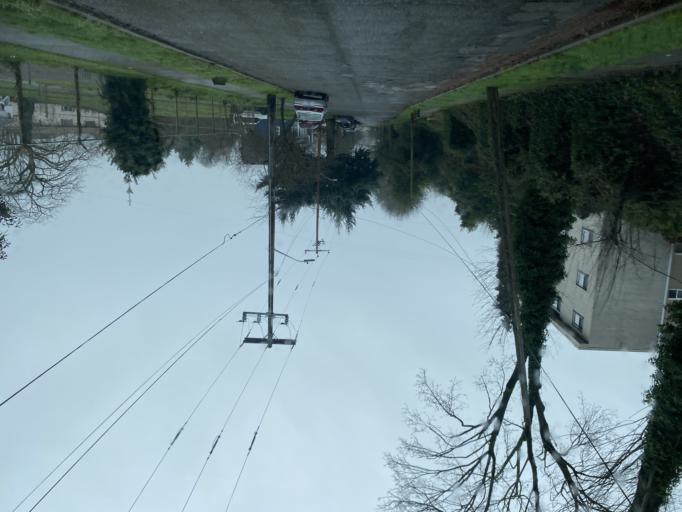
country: US
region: Washington
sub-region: King County
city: Seattle
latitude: 47.5986
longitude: -122.2951
